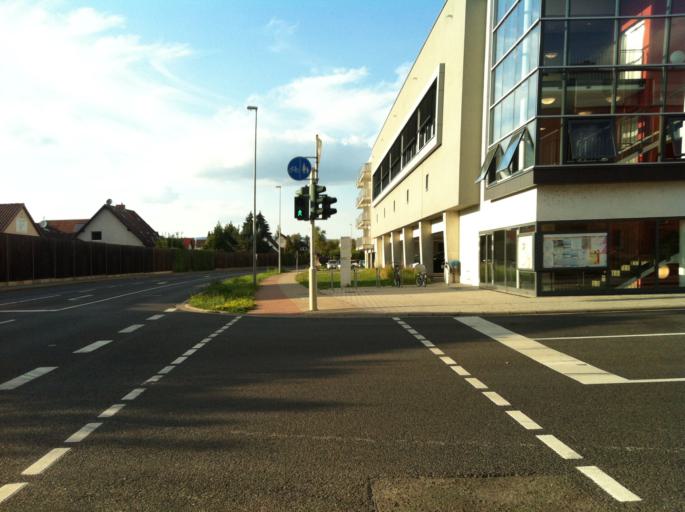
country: DE
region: Rheinland-Pfalz
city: Budenheim
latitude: 50.0070
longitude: 8.2160
